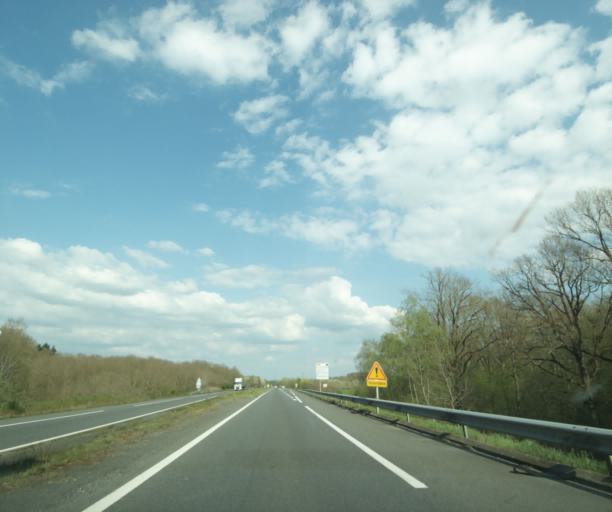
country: FR
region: Auvergne
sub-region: Departement de l'Allier
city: Dompierre-sur-Besbre
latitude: 46.5359
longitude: 3.6450
